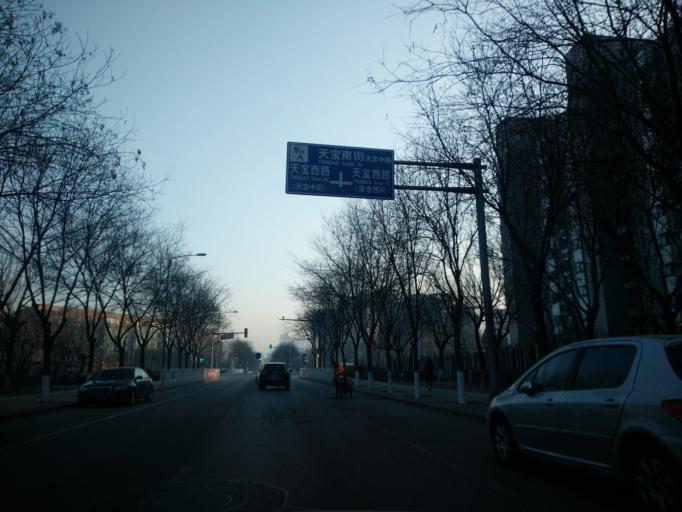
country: CN
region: Beijing
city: Jiugong
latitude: 39.7882
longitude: 116.4875
